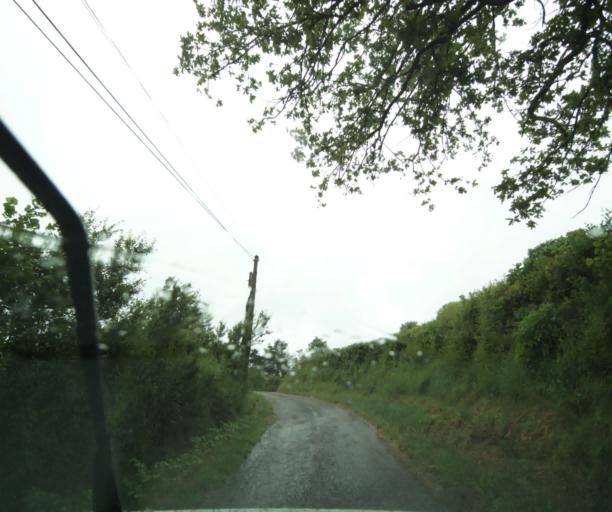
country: FR
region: Bourgogne
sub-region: Departement de Saone-et-Loire
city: Saint-Vallier
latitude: 46.4922
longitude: 4.4645
